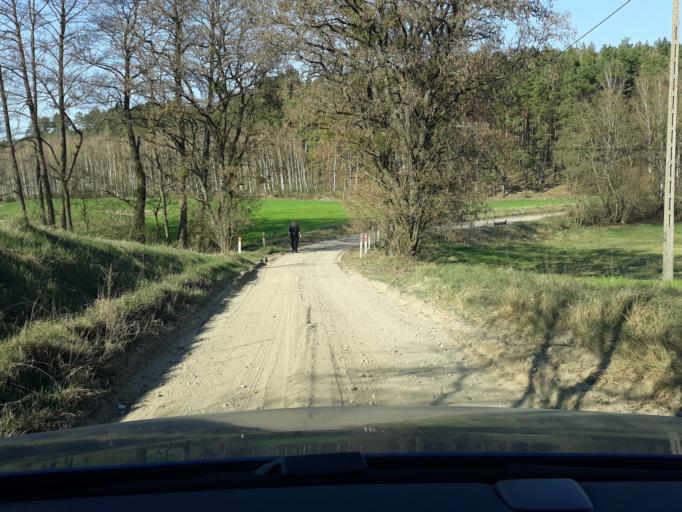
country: PL
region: Pomeranian Voivodeship
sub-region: Powiat bytowski
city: Lipnica
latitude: 53.9120
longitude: 17.4321
